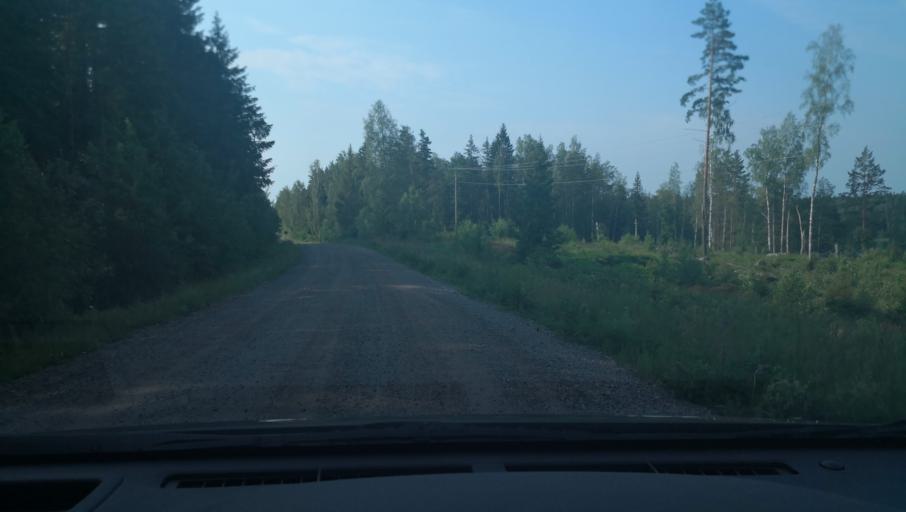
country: SE
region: Vaestmanland
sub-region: Arboga Kommun
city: Tyringe
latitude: 59.3686
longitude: 15.9535
